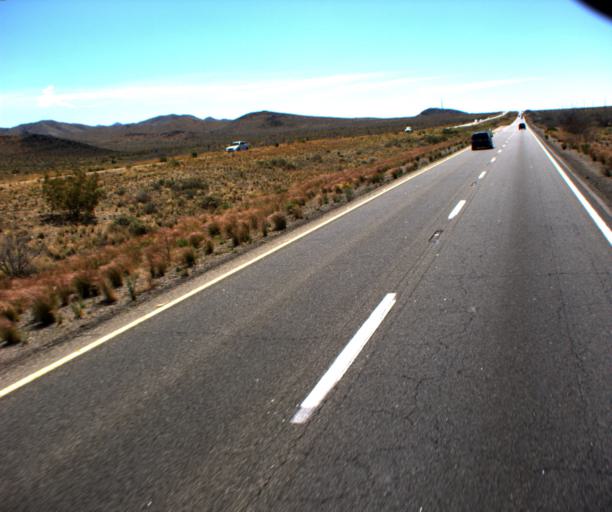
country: US
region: Arizona
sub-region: Mohave County
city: Dolan Springs
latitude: 35.4584
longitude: -114.3034
